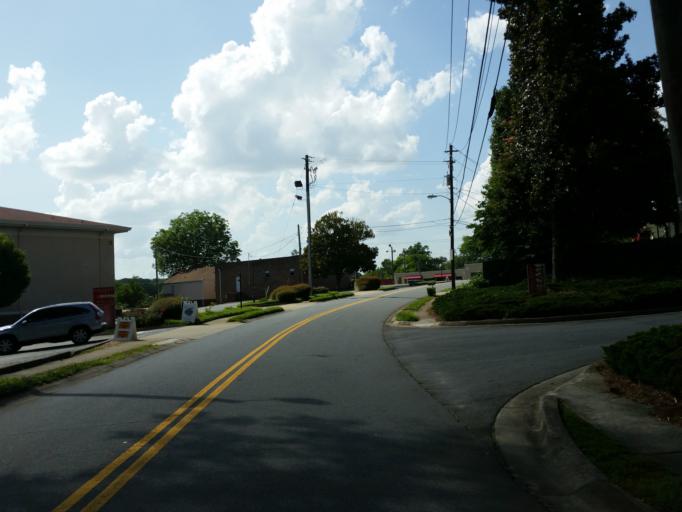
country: US
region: Georgia
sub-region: Cobb County
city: Marietta
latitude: 33.9498
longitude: -84.5274
